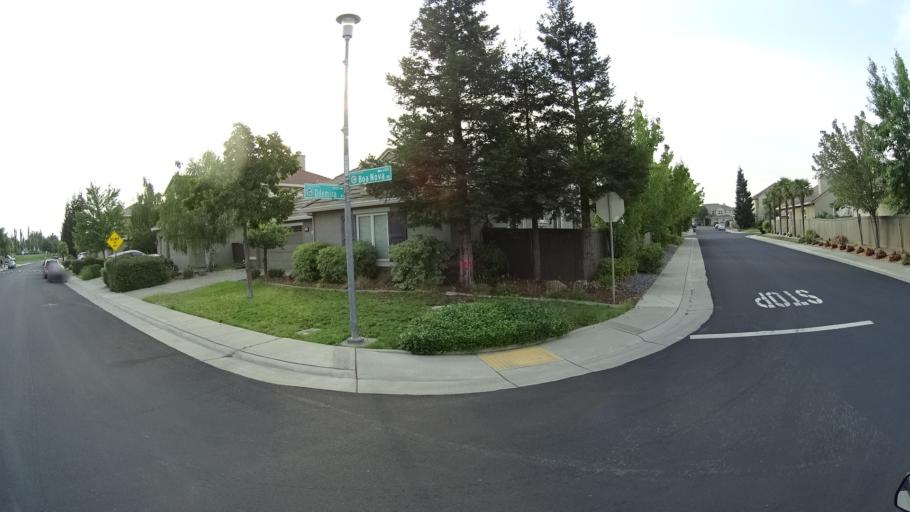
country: US
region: California
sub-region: Sacramento County
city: Laguna
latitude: 38.3824
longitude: -121.4224
